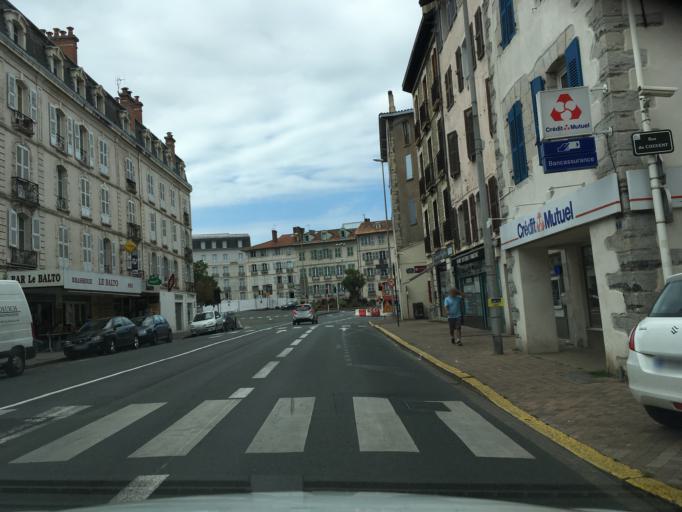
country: FR
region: Aquitaine
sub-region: Departement des Pyrenees-Atlantiques
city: Bayonne
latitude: 43.4950
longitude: -1.4691
